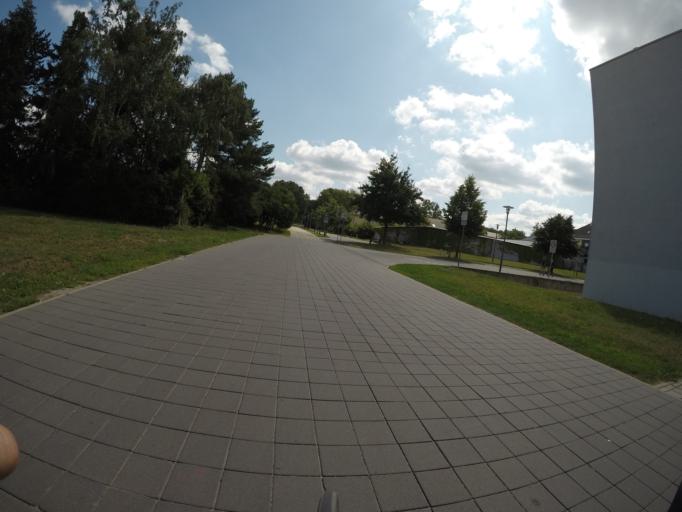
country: DE
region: Brandenburg
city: Werder
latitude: 52.4098
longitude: 12.9758
